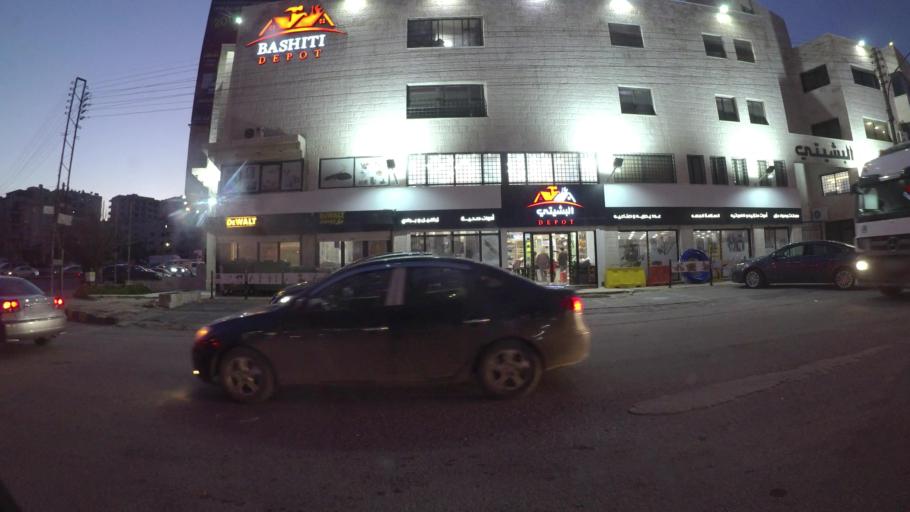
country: JO
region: Amman
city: Al Jubayhah
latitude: 31.9944
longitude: 35.8599
